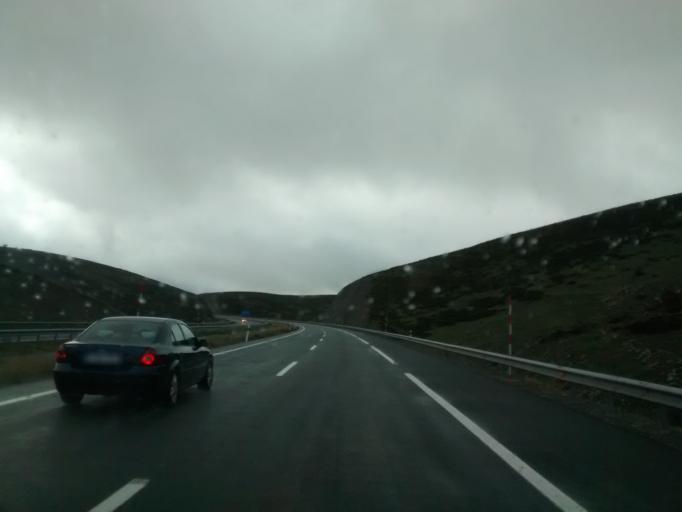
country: ES
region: Cantabria
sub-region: Provincia de Cantabria
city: Villaescusa
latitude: 42.9271
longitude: -4.1244
